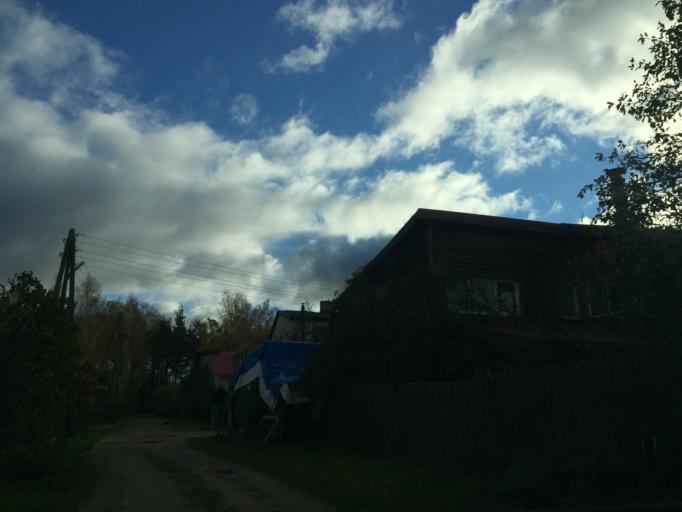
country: LV
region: Carnikava
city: Carnikava
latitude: 57.1452
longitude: 24.2686
